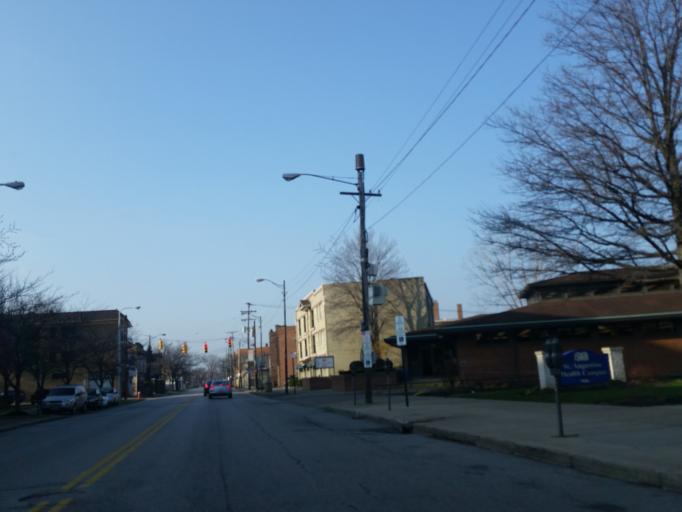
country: US
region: Ohio
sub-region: Cuyahoga County
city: Brooklyn
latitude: 41.4818
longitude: -81.7389
